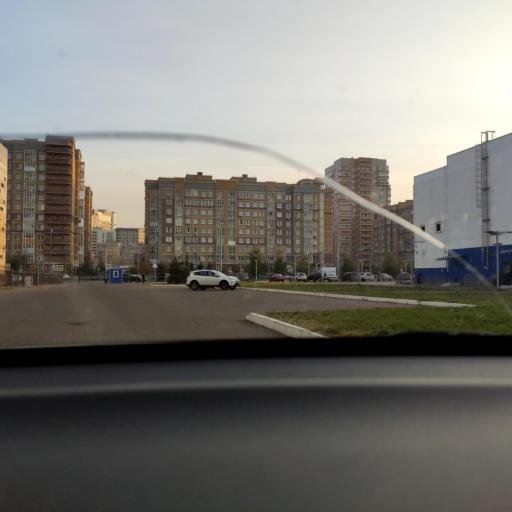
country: RU
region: Tatarstan
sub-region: Gorod Kazan'
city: Kazan
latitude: 55.8205
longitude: 49.1406
